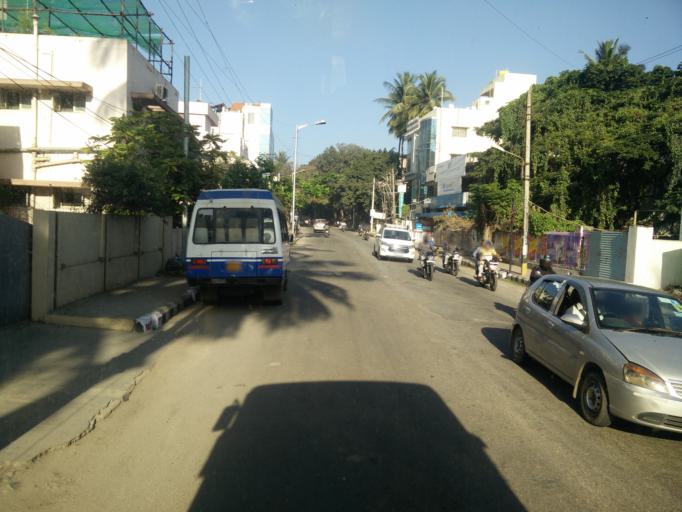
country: IN
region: Karnataka
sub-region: Bangalore Urban
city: Bangalore
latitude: 13.0023
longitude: 77.5986
